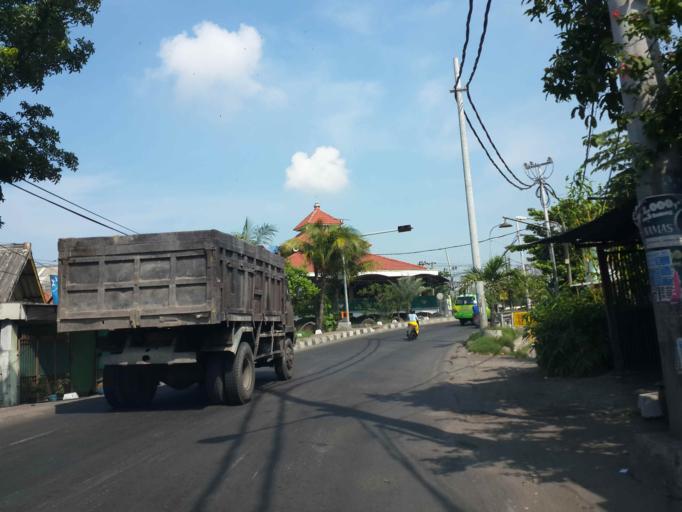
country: ID
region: East Java
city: Kebomas
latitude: -7.1957
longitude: 112.6452
